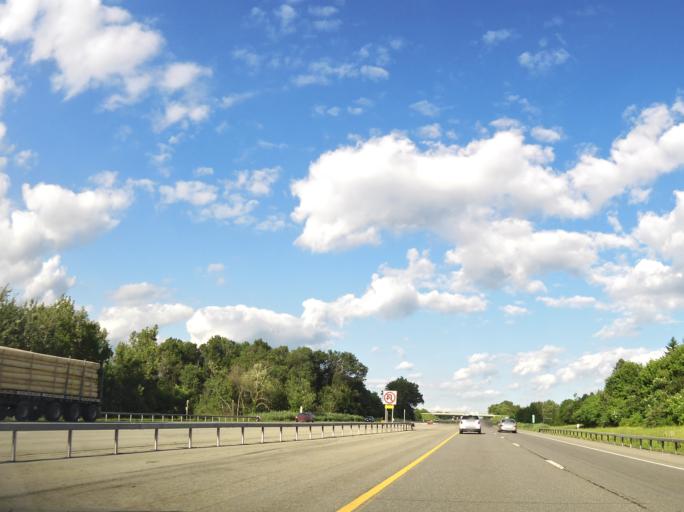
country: US
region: New York
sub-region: Genesee County
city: Oakfield
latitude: 43.0130
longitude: -78.3227
